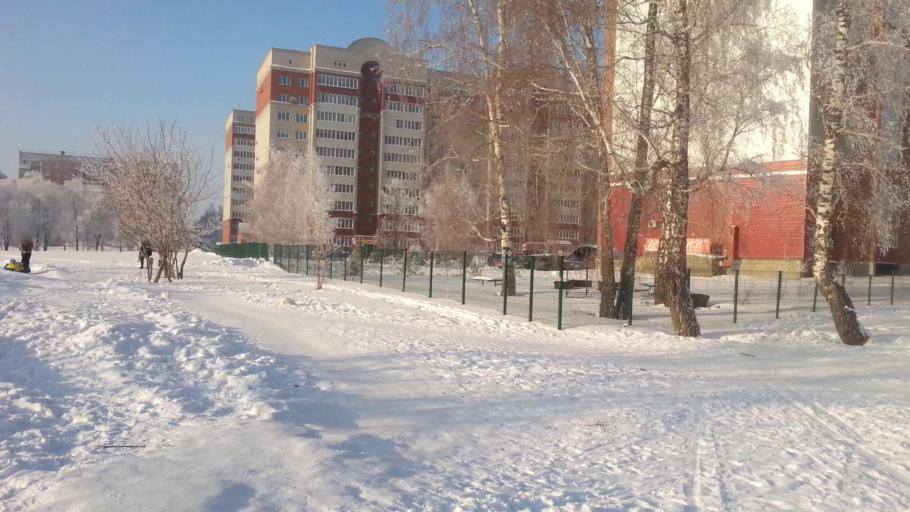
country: RU
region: Altai Krai
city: Novosilikatnyy
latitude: 53.3601
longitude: 83.6671
